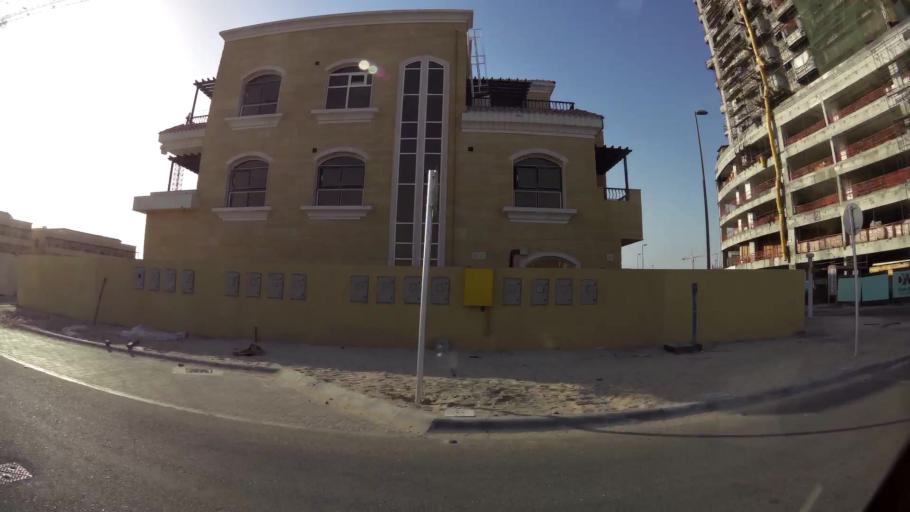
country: AE
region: Dubai
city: Dubai
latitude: 25.0601
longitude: 55.2142
